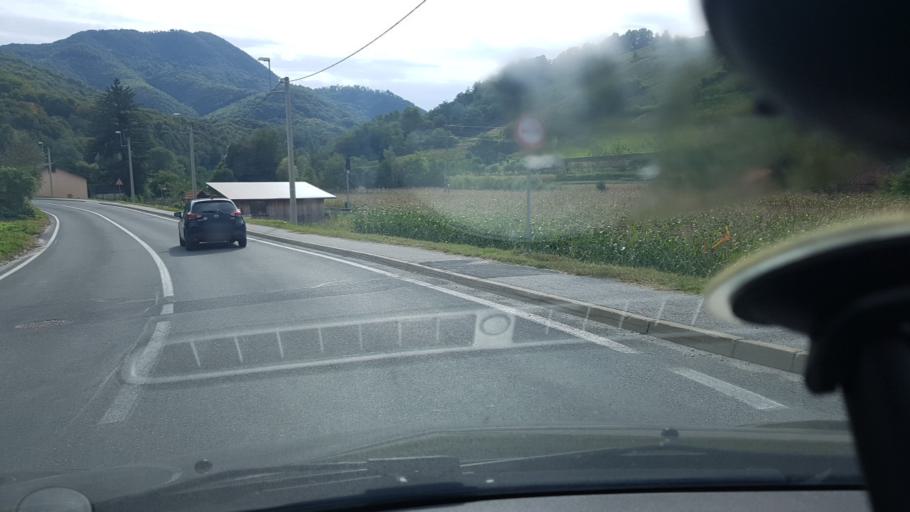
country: HR
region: Varazdinska
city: Lepoglava
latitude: 46.2041
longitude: 16.0237
